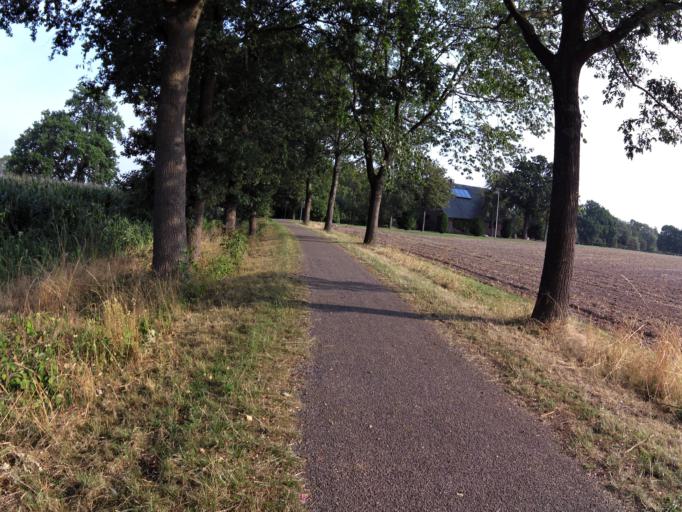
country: DE
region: North Rhine-Westphalia
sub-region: Regierungsbezirk Detmold
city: Petershagen
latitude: 52.4125
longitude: 8.9702
